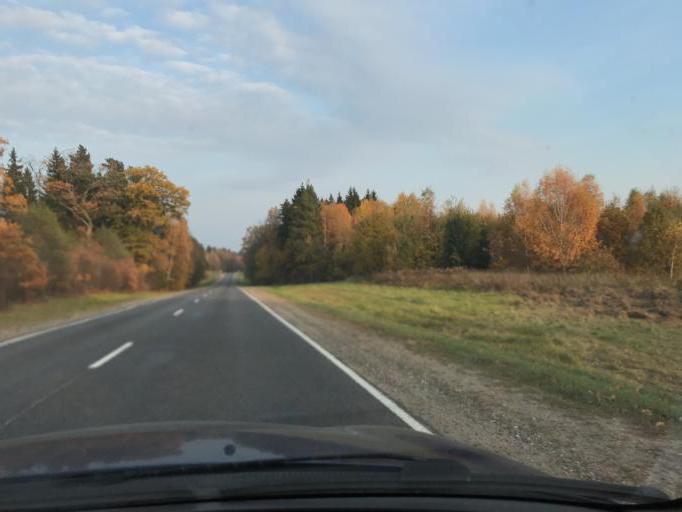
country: BY
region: Grodnenskaya
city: Navahrudak
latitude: 53.5903
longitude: 25.9111
